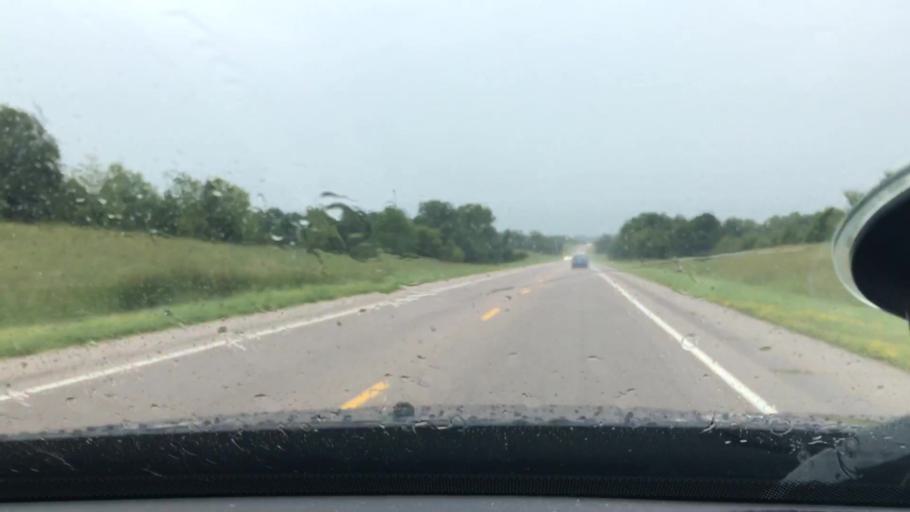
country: US
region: Oklahoma
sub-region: Seminole County
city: Maud
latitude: 35.0802
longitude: -96.6785
